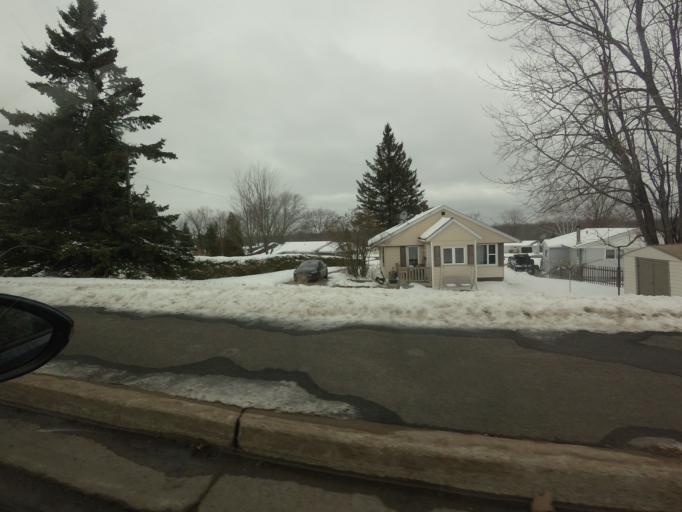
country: CA
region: New Brunswick
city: Oromocto
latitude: 45.8494
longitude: -66.4897
